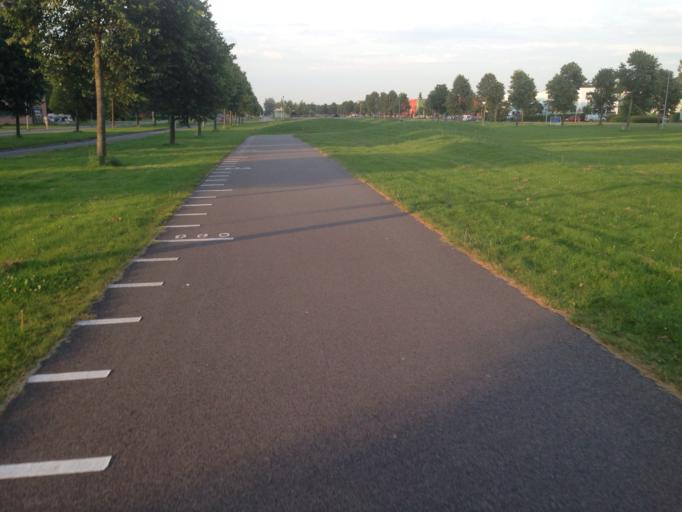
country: NL
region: Flevoland
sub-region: Gemeente Almere
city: Almere Stad
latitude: 52.3964
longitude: 5.2890
